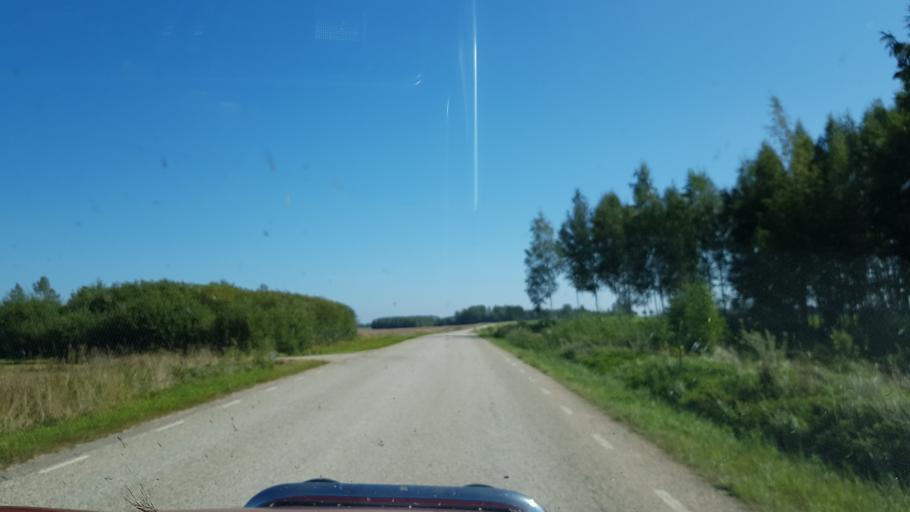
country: EE
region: Polvamaa
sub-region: Raepina vald
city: Rapina
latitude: 58.2337
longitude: 27.3354
